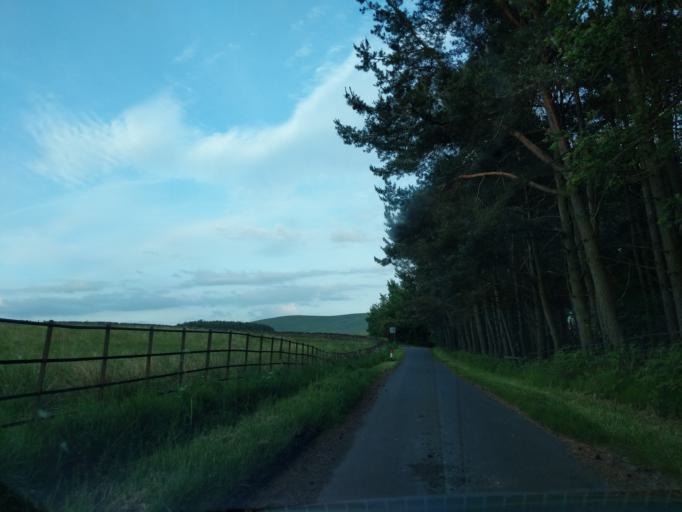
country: GB
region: Scotland
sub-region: Midlothian
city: Gorebridge
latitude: 55.7773
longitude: -3.1044
